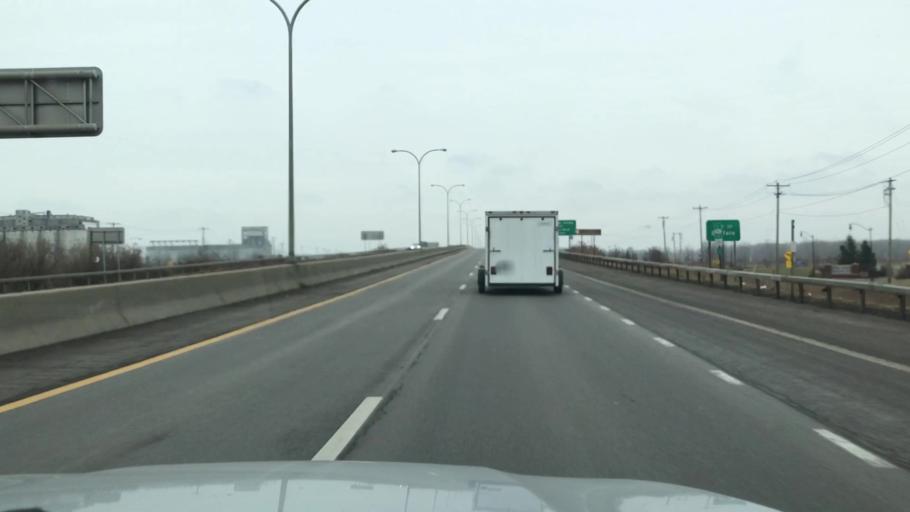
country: US
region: New York
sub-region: Erie County
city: Lackawanna
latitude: 42.8320
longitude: -78.8529
